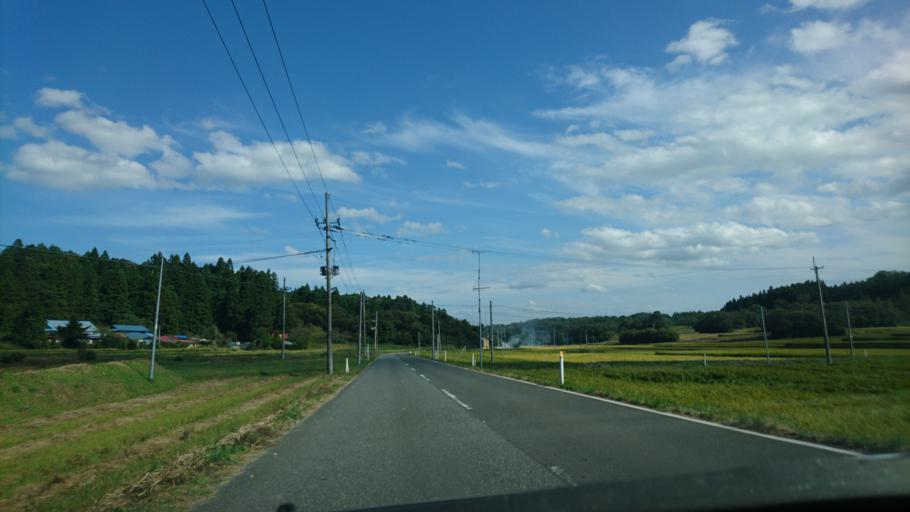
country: JP
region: Iwate
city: Ichinoseki
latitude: 38.8758
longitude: 141.0730
